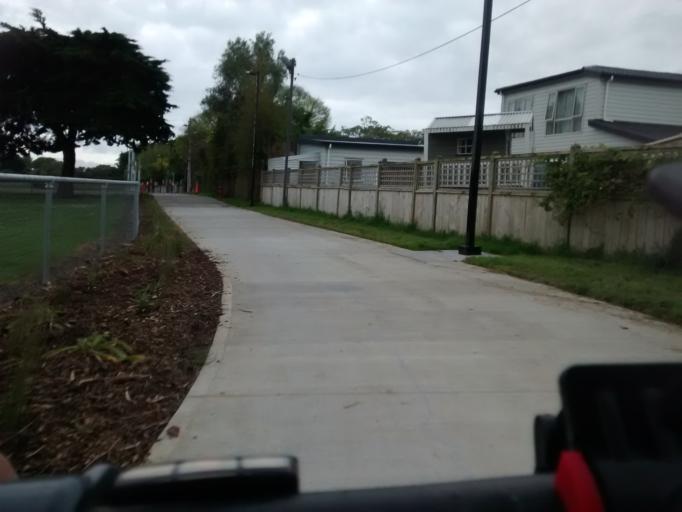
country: NZ
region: Auckland
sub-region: Auckland
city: Rosebank
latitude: -36.8869
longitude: 174.7047
